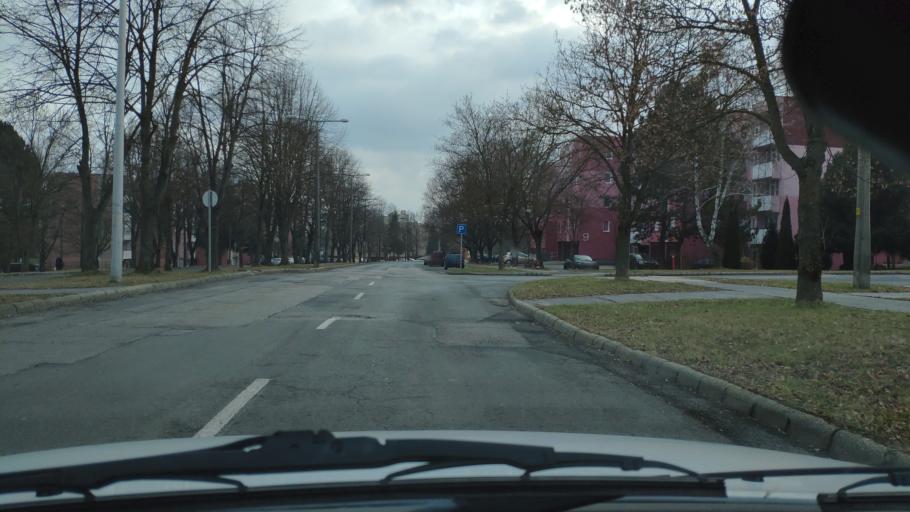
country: HU
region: Zala
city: Nagykanizsa
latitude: 46.4625
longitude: 17.0176
